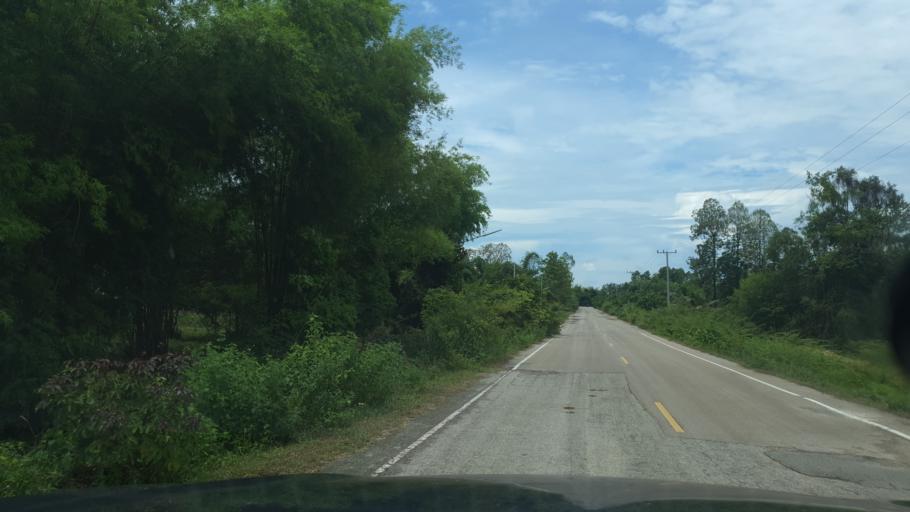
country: TH
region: Lampang
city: Ko Kha
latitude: 18.2391
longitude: 99.3693
